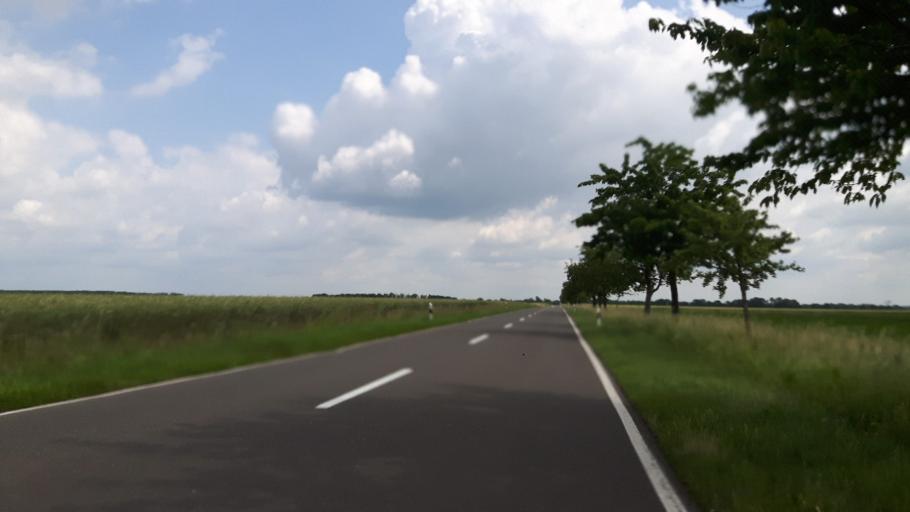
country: DE
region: Saxony
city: Delitzsch
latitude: 51.5445
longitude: 12.3692
